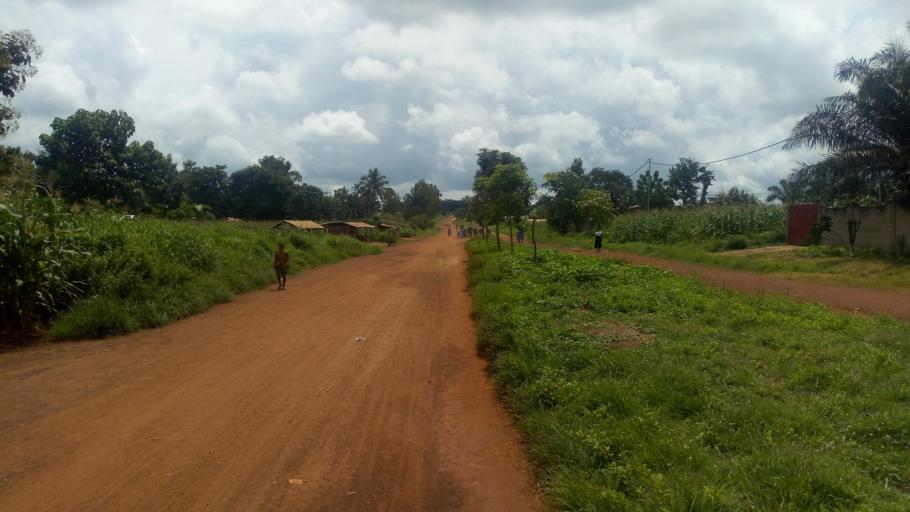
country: TG
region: Centrale
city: Sotouboua
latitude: 8.5553
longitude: 0.9888
